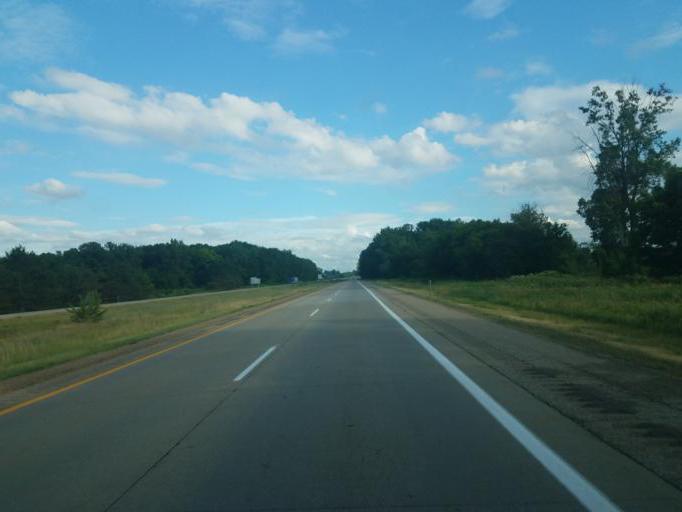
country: US
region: Indiana
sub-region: Steuben County
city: Fremont
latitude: 41.7813
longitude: -84.9909
